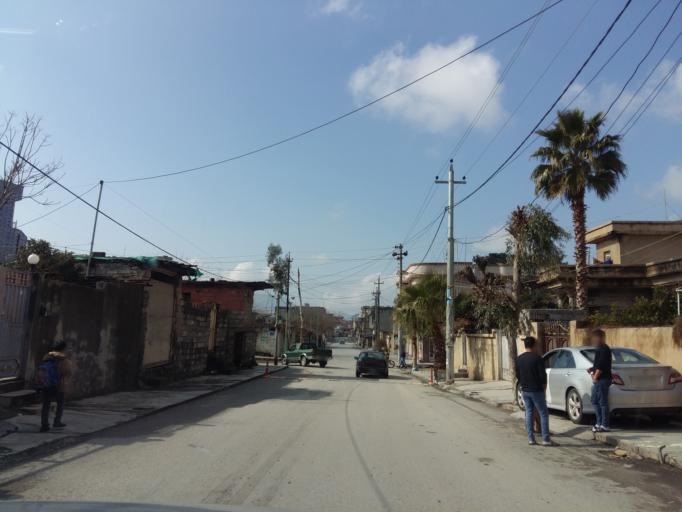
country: IQ
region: As Sulaymaniyah
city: Qeladize
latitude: 36.1867
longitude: 45.1226
